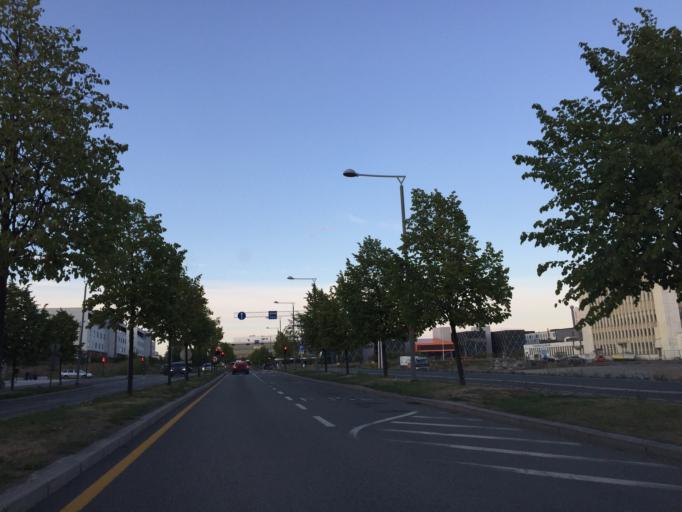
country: NO
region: Akershus
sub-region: Baerum
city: Lysaker
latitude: 59.8930
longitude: 10.6208
